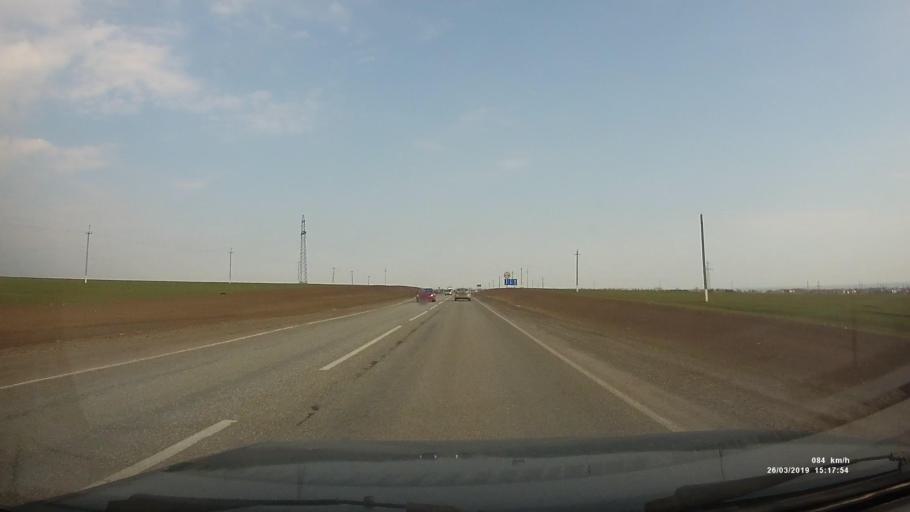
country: RU
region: Rostov
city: Taganrog
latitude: 47.2869
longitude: 38.9287
